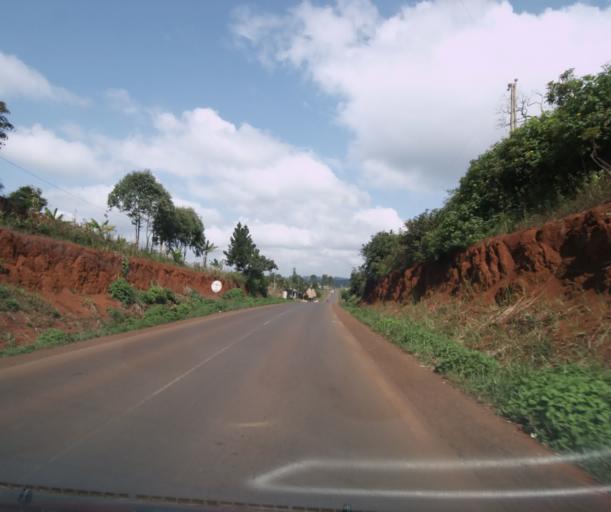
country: CM
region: West
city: Dschang
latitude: 5.4896
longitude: 10.1816
